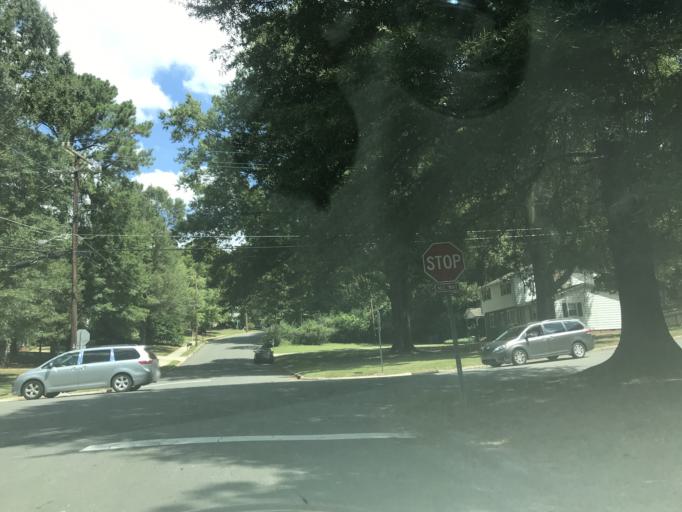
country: US
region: North Carolina
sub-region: Orange County
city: Chapel Hill
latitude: 35.9279
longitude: -79.0188
